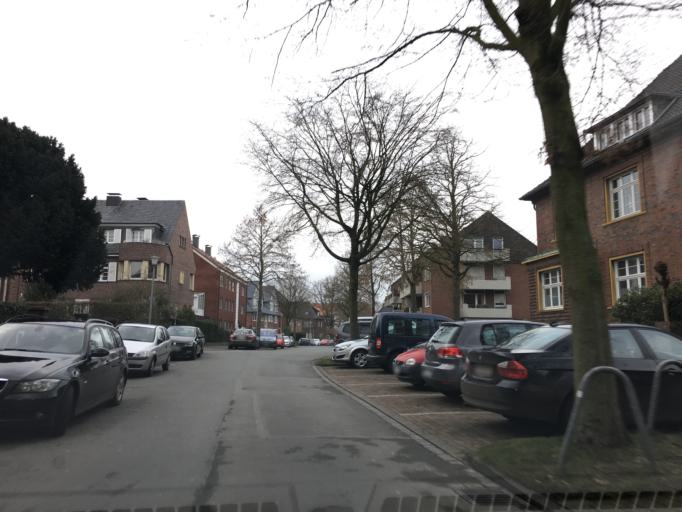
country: DE
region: North Rhine-Westphalia
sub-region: Regierungsbezirk Munster
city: Muenster
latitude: 51.9697
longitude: 7.6175
